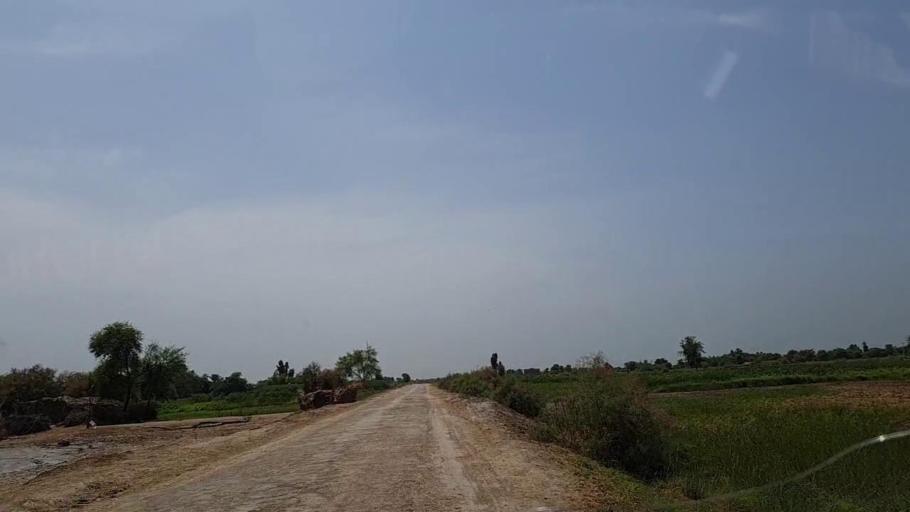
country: PK
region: Sindh
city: Khanpur
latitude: 27.8668
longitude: 69.4882
